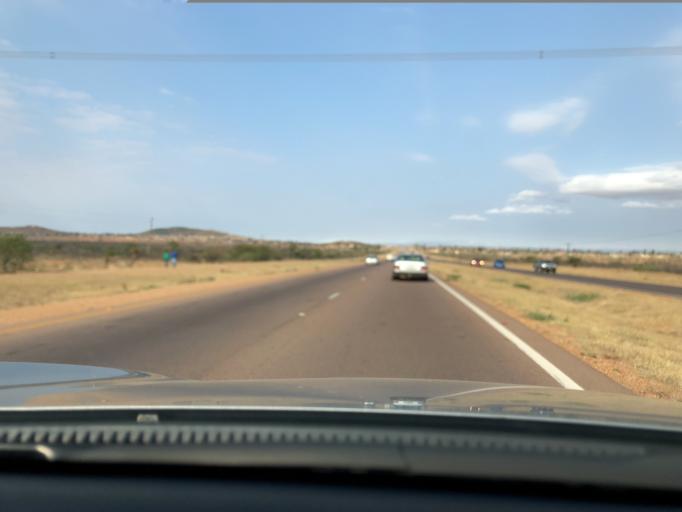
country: ZA
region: Limpopo
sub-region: Capricorn District Municipality
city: Polokwane
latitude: -23.8944
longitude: 29.6383
